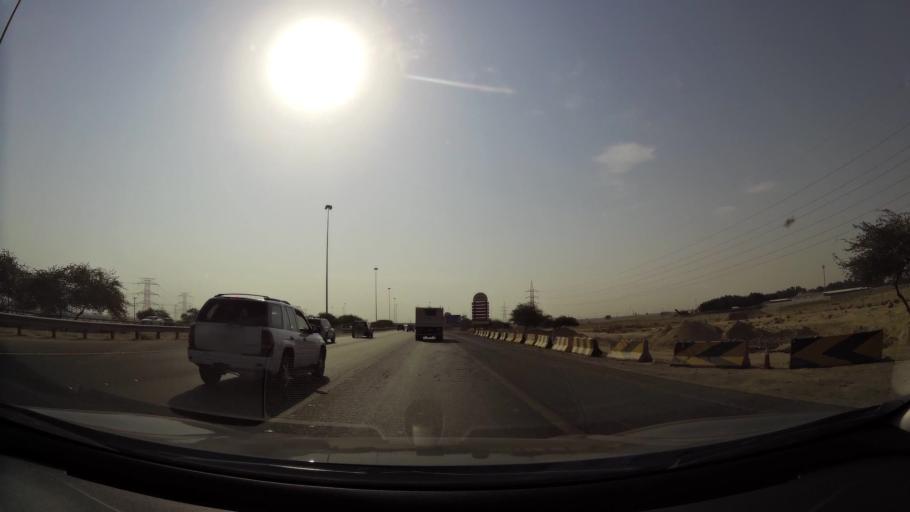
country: KW
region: Al Ahmadi
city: Al Ahmadi
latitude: 28.9656
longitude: 48.1171
